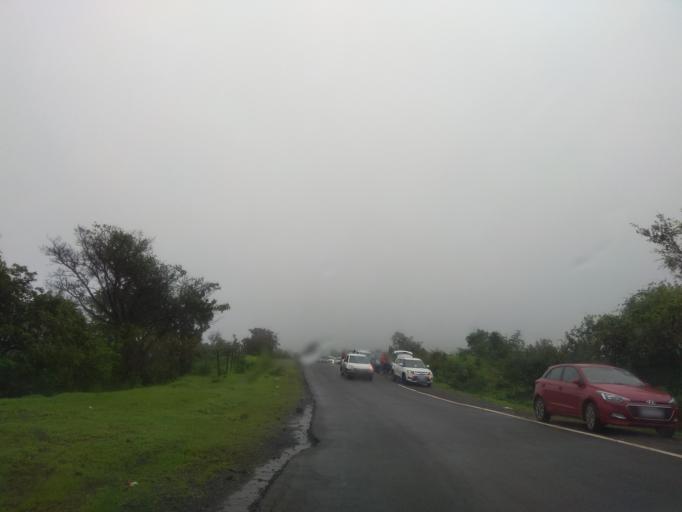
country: IN
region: Maharashtra
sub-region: Raigarh
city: Indapur
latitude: 18.4919
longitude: 73.4239
